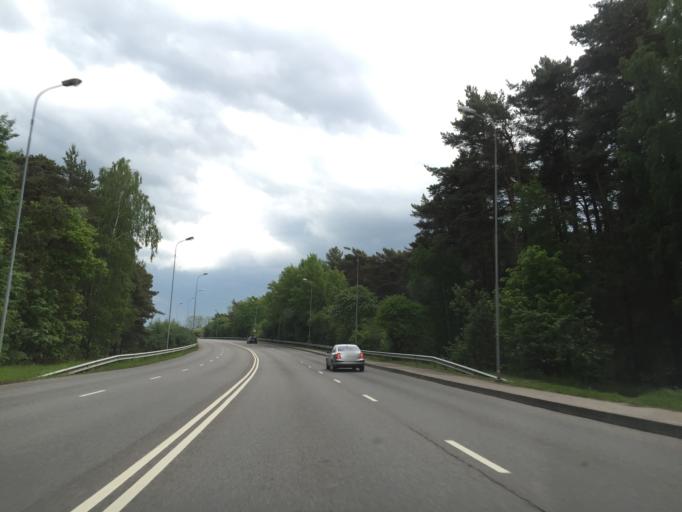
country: LT
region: Klaipedos apskritis
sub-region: Klaipeda
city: Klaipeda
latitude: 55.7350
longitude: 21.1016
